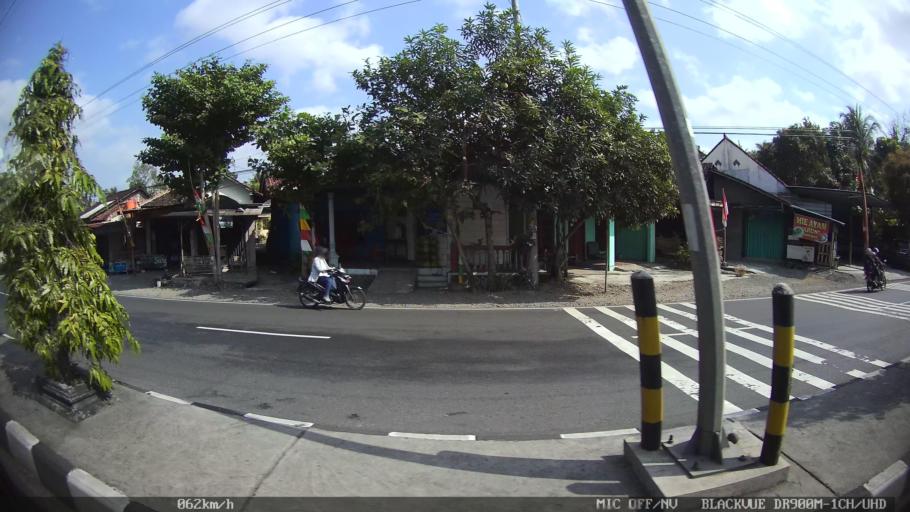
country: ID
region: Daerah Istimewa Yogyakarta
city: Srandakan
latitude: -7.8560
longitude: 110.2150
